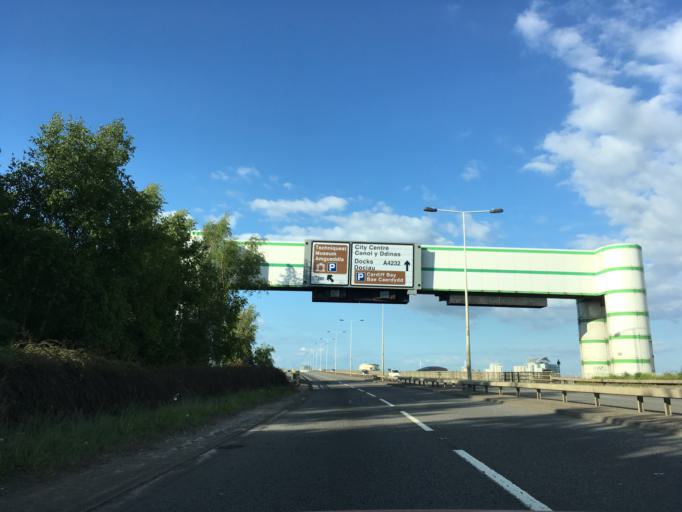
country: GB
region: Wales
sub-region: Vale of Glamorgan
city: Penarth
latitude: 51.4554
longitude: -3.1798
